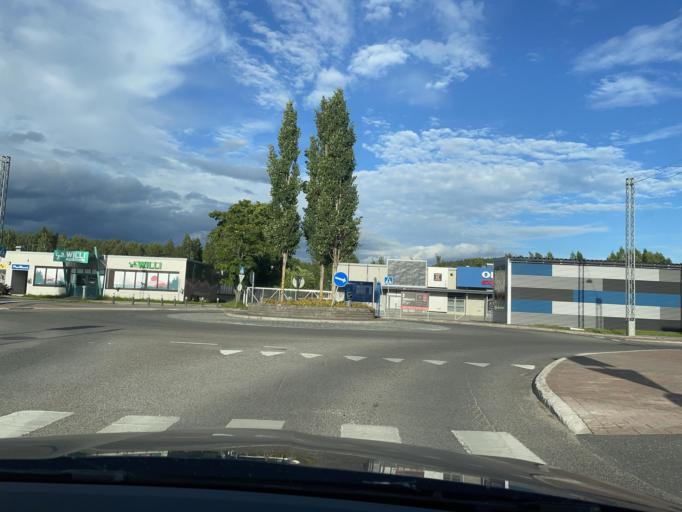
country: FI
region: Central Finland
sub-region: Jyvaeskylae
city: Jyvaeskylae
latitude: 62.2566
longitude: 25.7771
